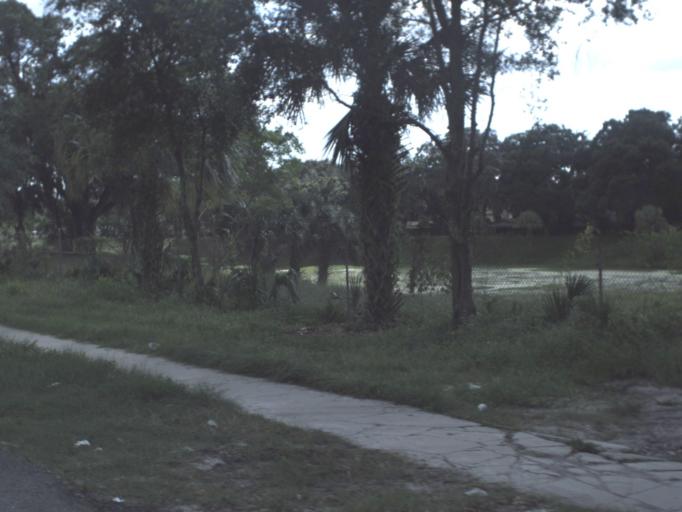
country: US
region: Florida
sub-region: Hillsborough County
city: Tampa
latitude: 27.9873
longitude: -82.4348
